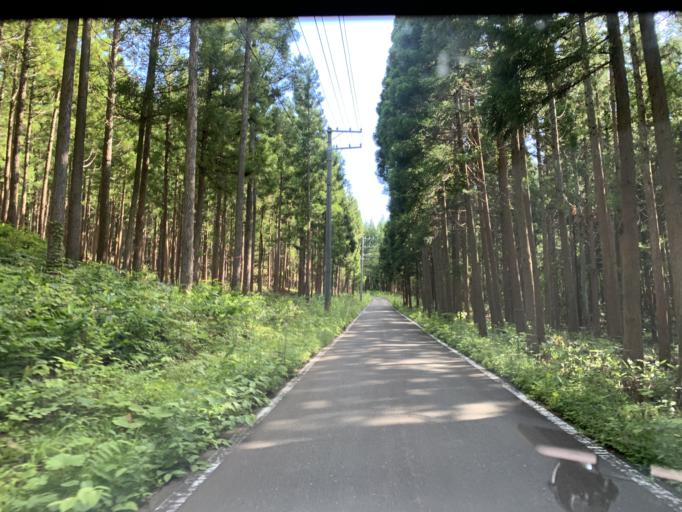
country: JP
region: Iwate
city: Ichinoseki
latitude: 38.8947
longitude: 140.9075
